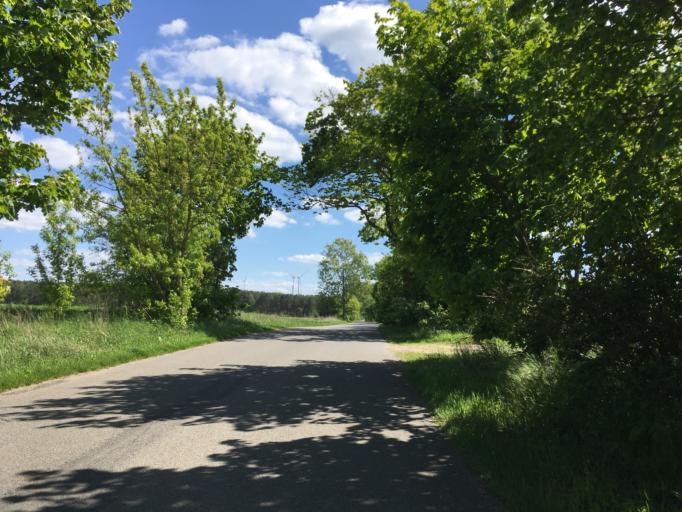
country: DE
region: Brandenburg
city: Rudnitz
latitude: 52.7030
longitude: 13.6632
